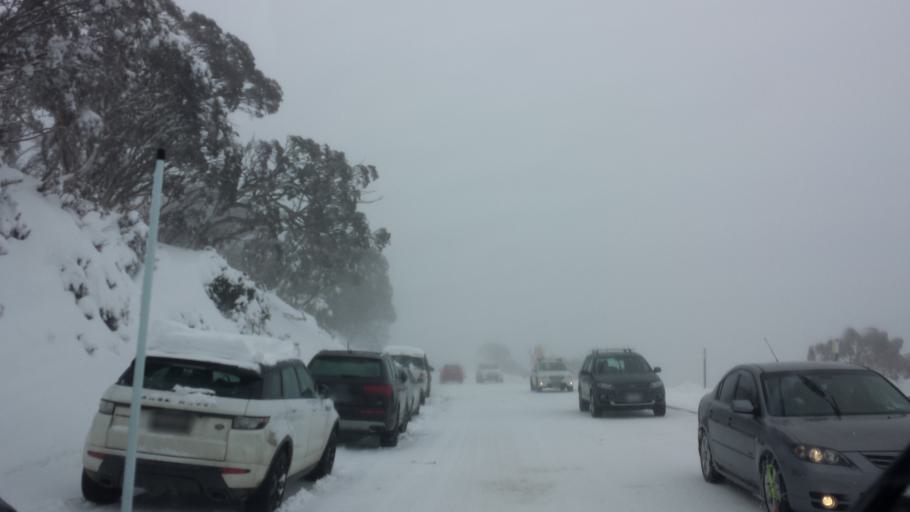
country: AU
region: Victoria
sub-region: Alpine
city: Mount Beauty
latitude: -36.9873
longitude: 147.1480
